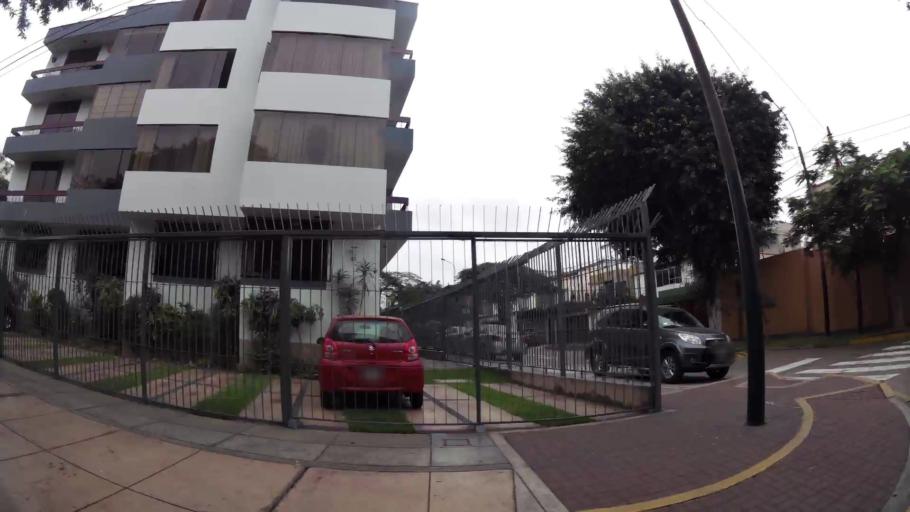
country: PE
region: Lima
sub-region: Lima
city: San Luis
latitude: -12.1013
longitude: -77.0159
